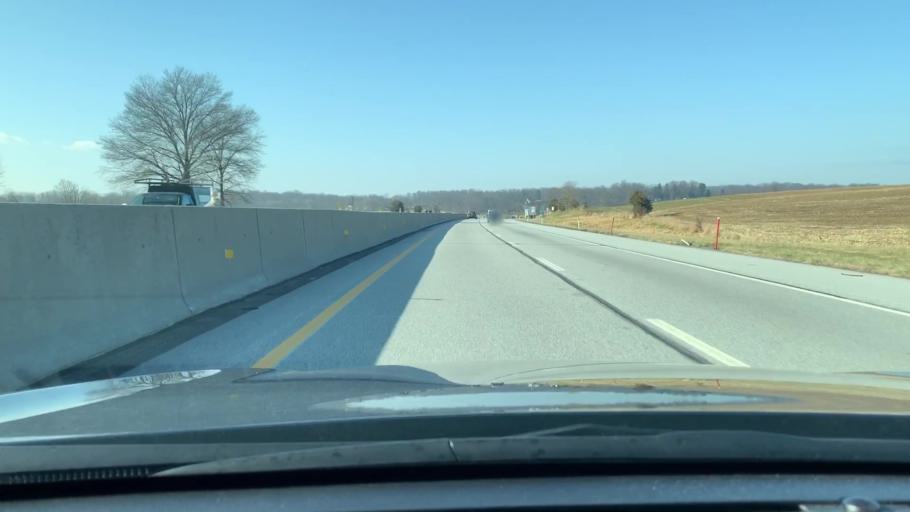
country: US
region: Pennsylvania
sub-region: Lancaster County
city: Elizabethtown
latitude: 40.2078
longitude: -76.6049
